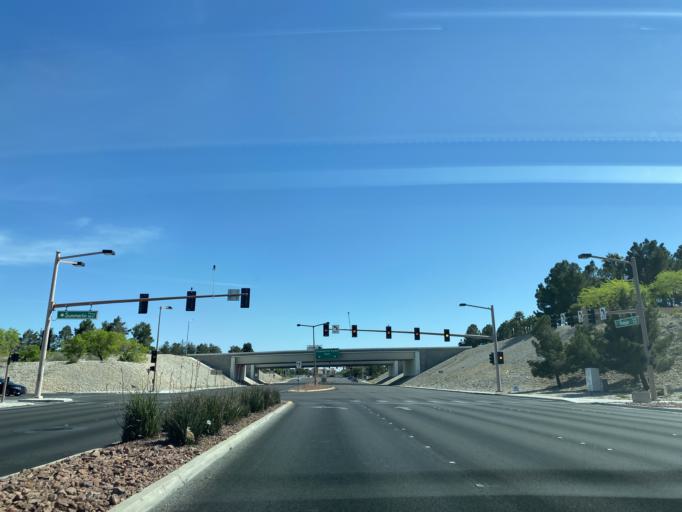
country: US
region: Nevada
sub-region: Clark County
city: Summerlin South
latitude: 36.1795
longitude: -115.2873
